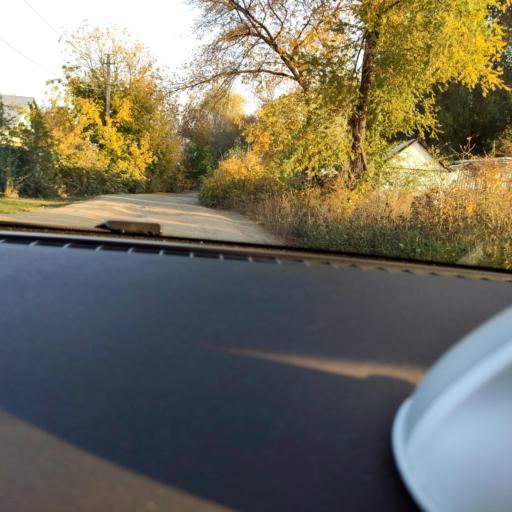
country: RU
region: Samara
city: Samara
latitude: 53.2169
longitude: 50.2149
